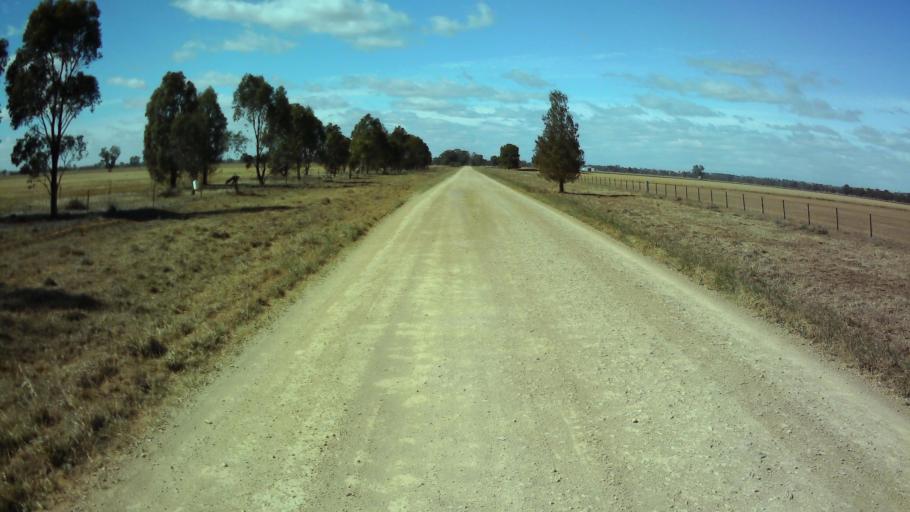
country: AU
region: New South Wales
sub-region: Weddin
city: Grenfell
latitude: -34.0189
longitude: 148.3194
